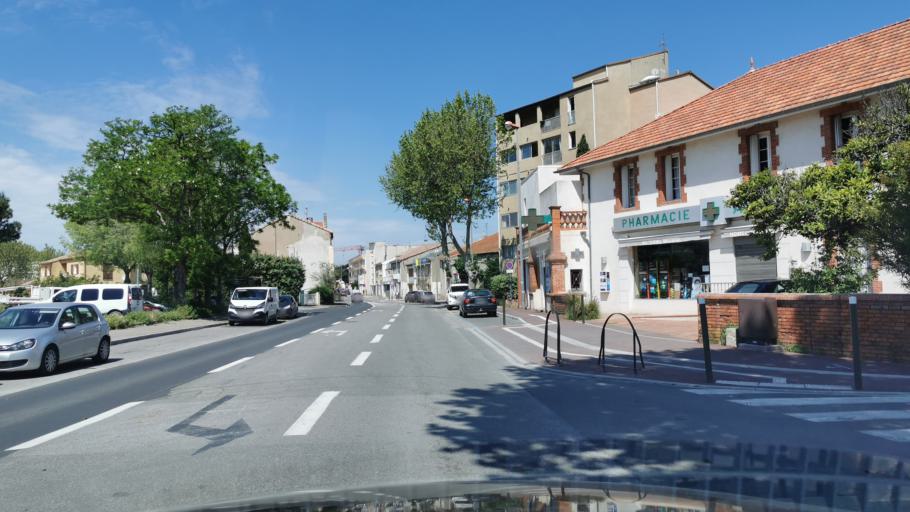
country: FR
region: Languedoc-Roussillon
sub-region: Departement de l'Aude
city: Narbonne
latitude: 43.1856
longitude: 2.9936
